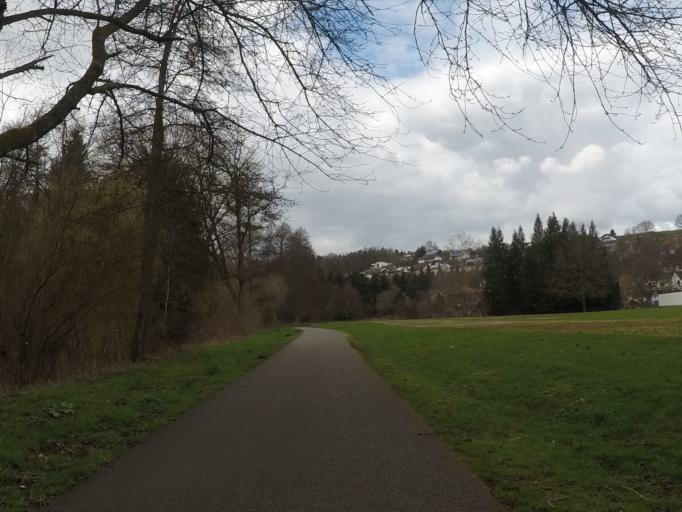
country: DE
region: Rheinland-Pfalz
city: Rieschweiler-Muhlbach
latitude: 49.2473
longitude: 7.5138
